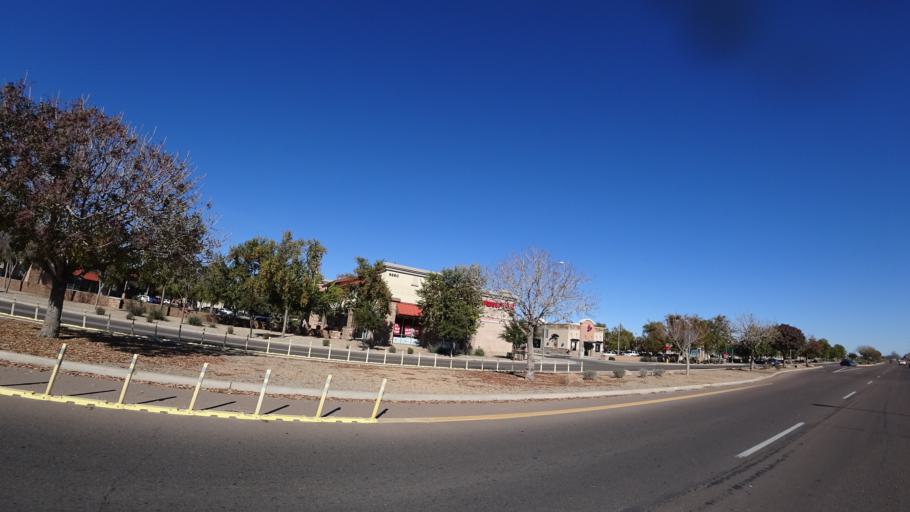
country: US
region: Arizona
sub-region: Maricopa County
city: Tolleson
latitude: 33.4210
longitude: -112.2717
